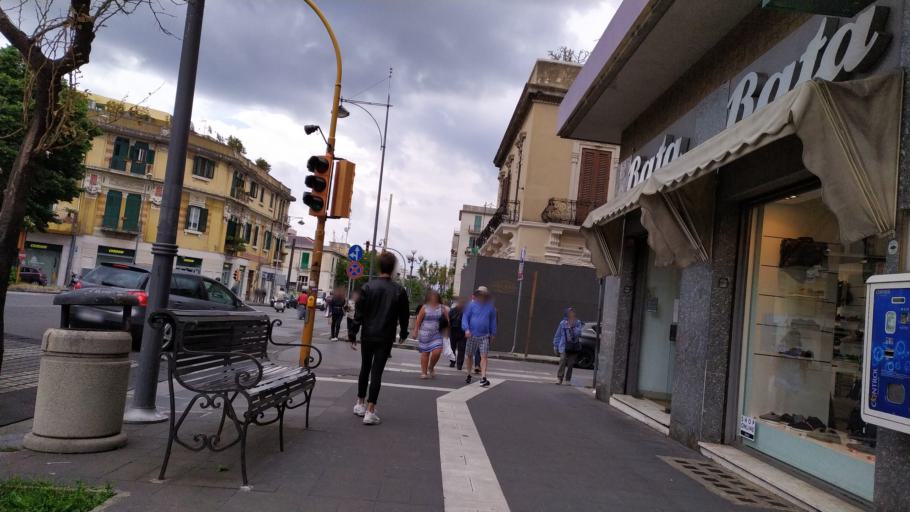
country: IT
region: Sicily
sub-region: Messina
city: Messina
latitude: 38.1869
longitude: 15.5557
